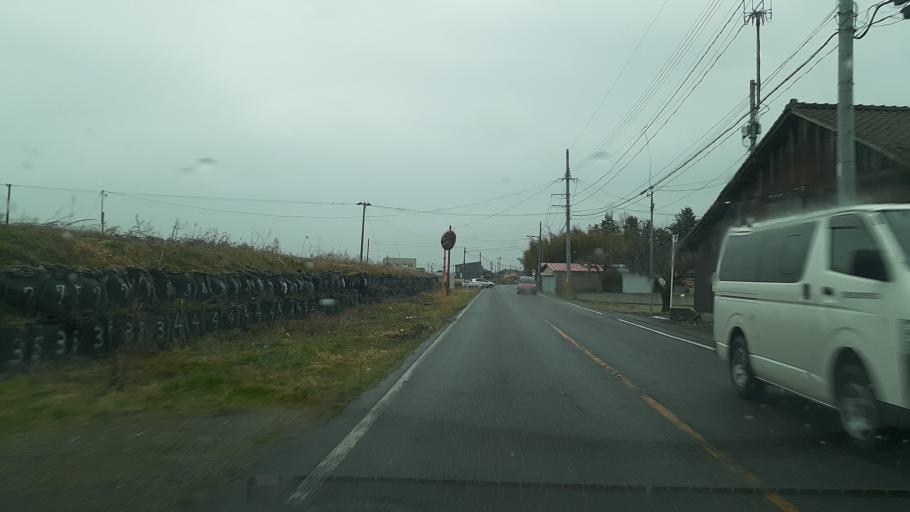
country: JP
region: Niigata
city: Kameda-honcho
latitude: 37.8778
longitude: 139.1220
